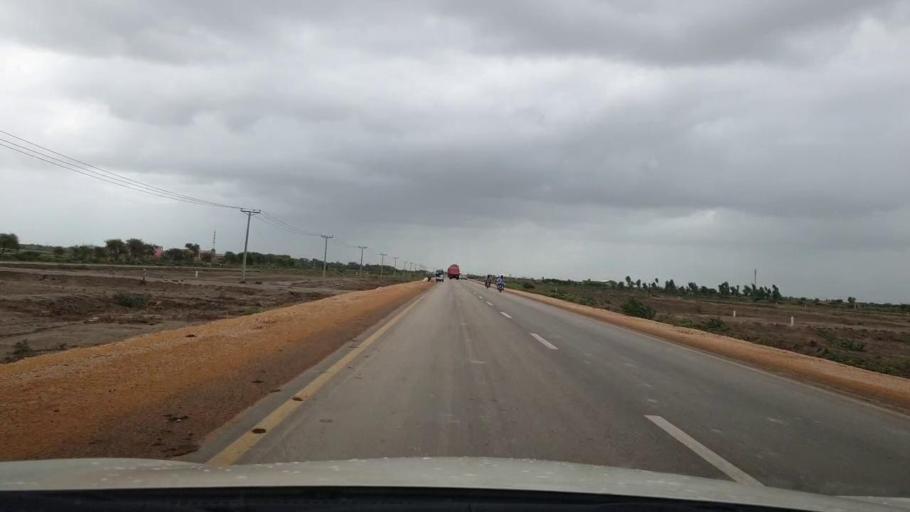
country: PK
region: Sindh
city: Badin
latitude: 24.6544
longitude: 68.7557
